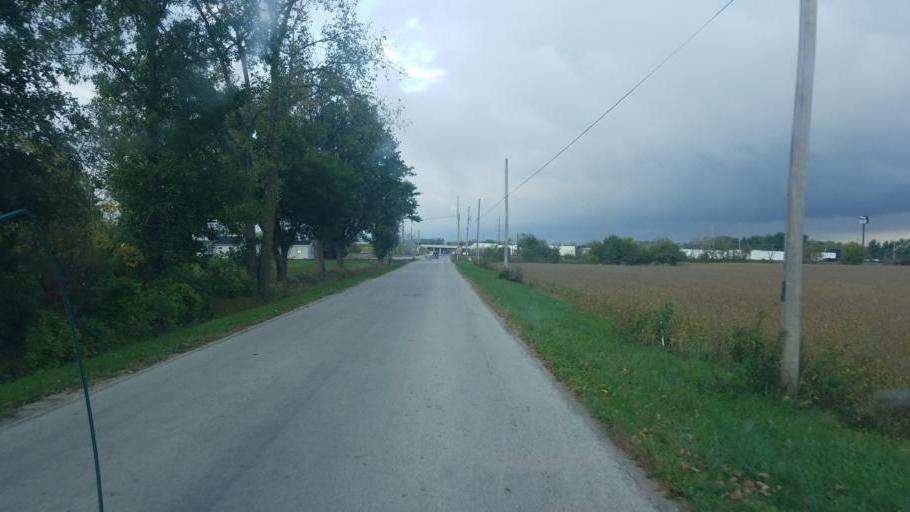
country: US
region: Ohio
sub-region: Wood County
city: North Baltimore
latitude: 41.1822
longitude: -83.6431
